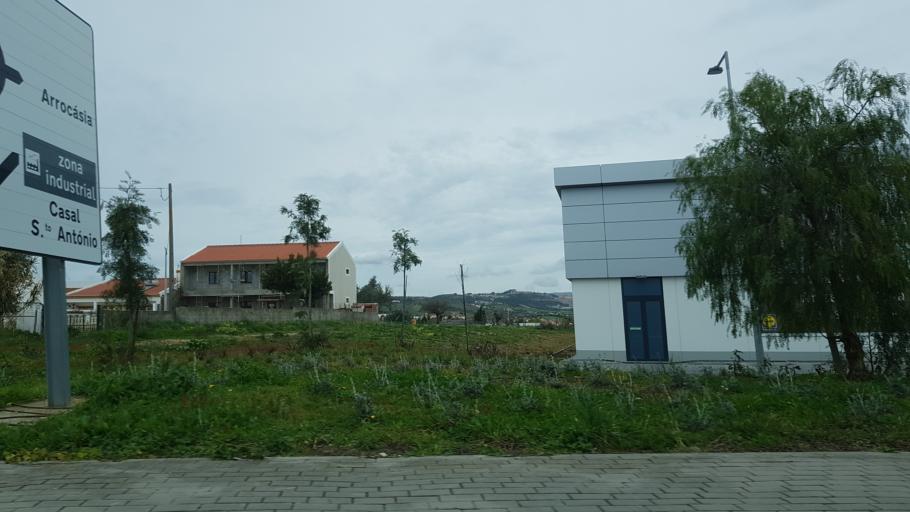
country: PT
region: Lisbon
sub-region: Alenquer
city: Carregado
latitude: 39.0402
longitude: -8.9883
